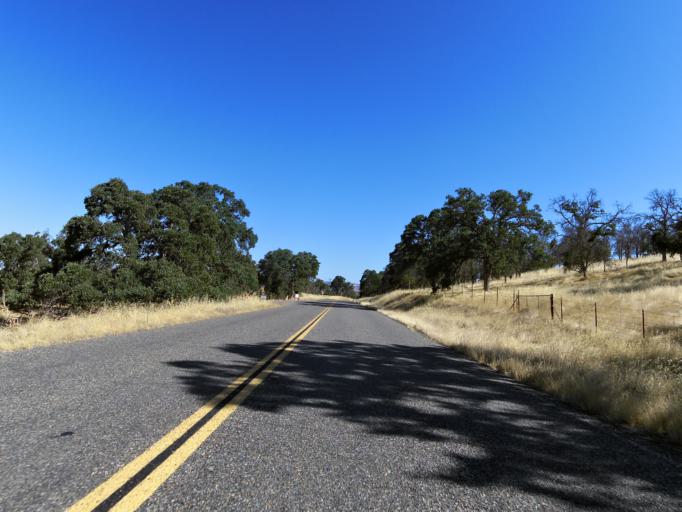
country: US
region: California
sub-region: Mariposa County
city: Mariposa
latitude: 37.4565
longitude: -120.1041
